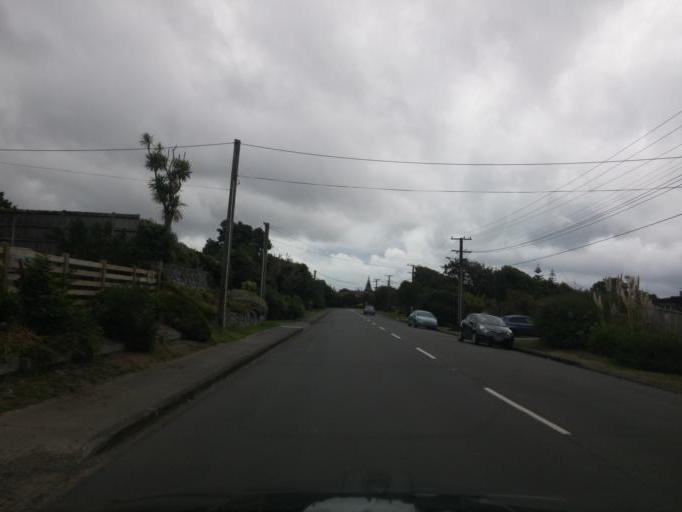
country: NZ
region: Wellington
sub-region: Kapiti Coast District
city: Paraparaumu
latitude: -40.8666
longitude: 175.0253
